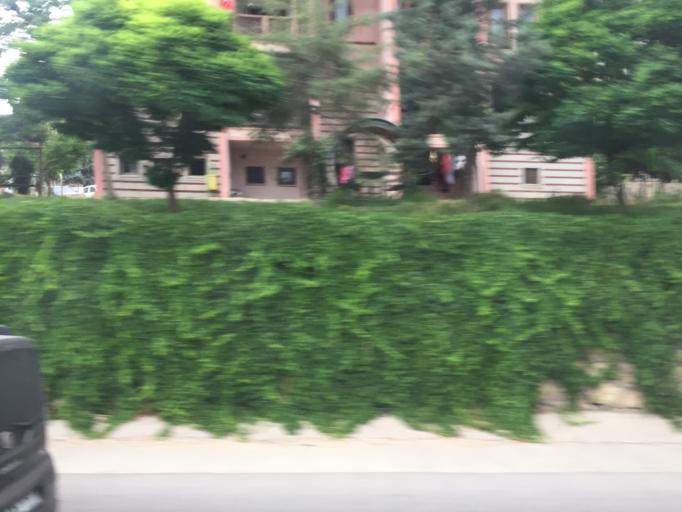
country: TR
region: Gaziantep
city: Gaziantep
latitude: 37.0508
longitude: 37.4213
